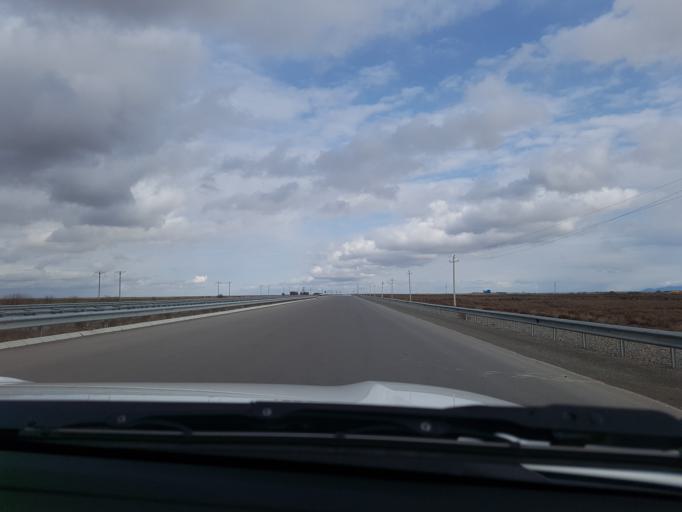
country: TM
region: Balkan
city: Gazanjyk
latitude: 39.2490
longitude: 55.6217
